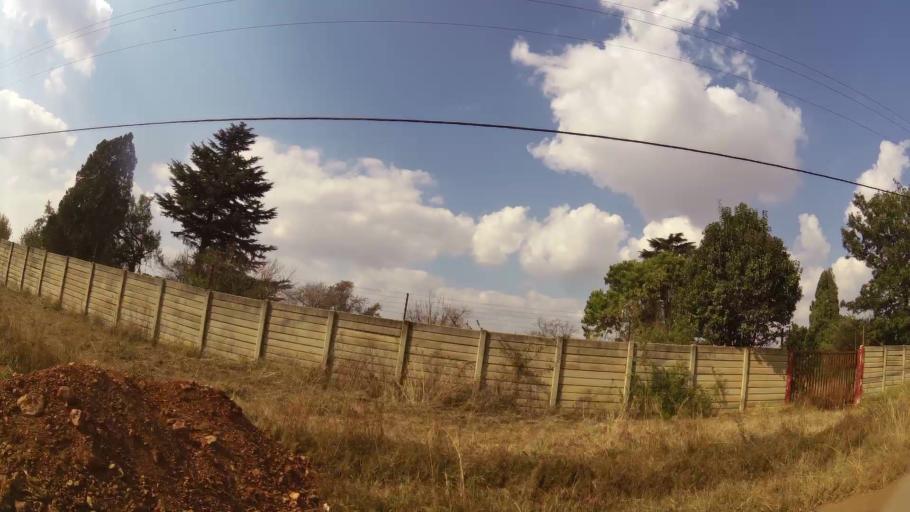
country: ZA
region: Mpumalanga
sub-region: Nkangala District Municipality
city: Delmas
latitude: -26.1515
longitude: 28.5448
